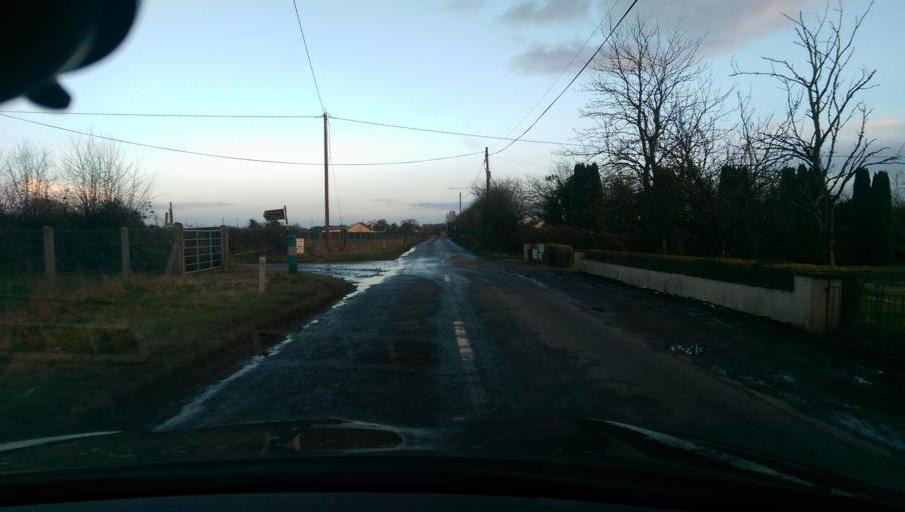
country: IE
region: Connaught
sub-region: County Galway
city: Ballinasloe
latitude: 53.3831
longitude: -8.2960
